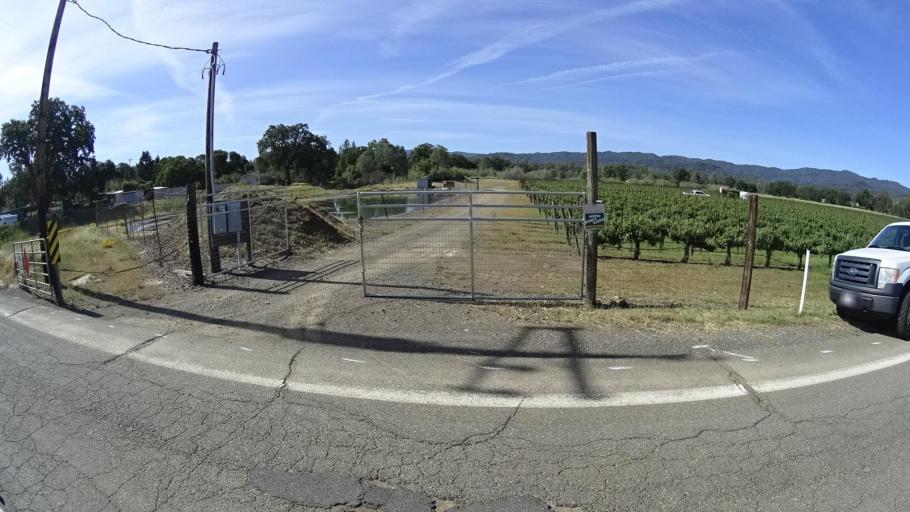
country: US
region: California
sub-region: Lake County
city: Kelseyville
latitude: 38.9574
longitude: -122.8918
